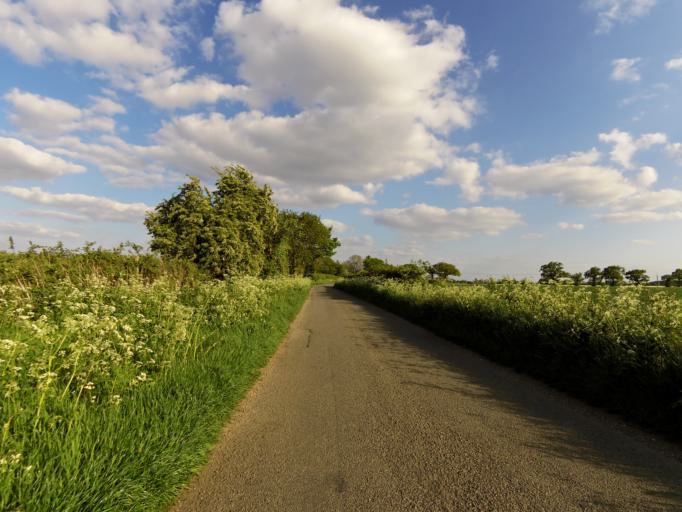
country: GB
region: England
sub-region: Suffolk
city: Halesworth
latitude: 52.3989
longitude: 1.5106
